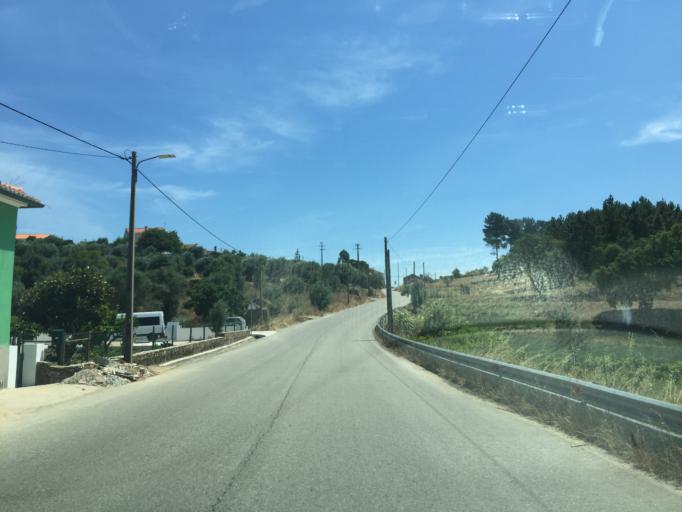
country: PT
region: Santarem
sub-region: Tomar
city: Tomar
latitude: 39.5960
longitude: -8.3289
